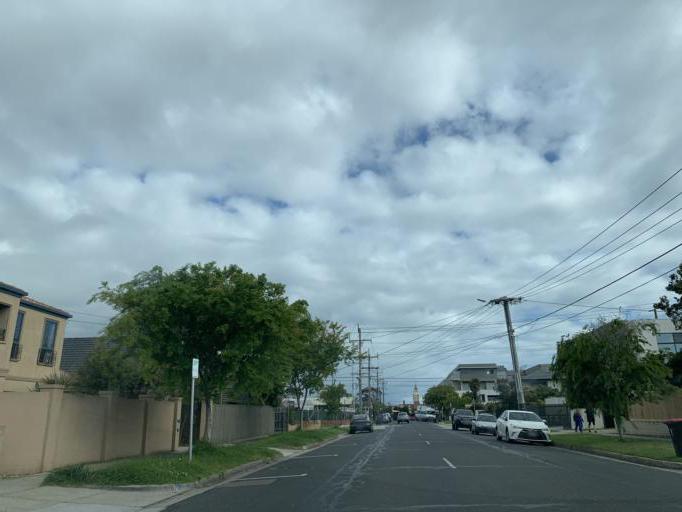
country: AU
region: Victoria
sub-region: Kingston
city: Mentone
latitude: -37.9796
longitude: 145.0659
